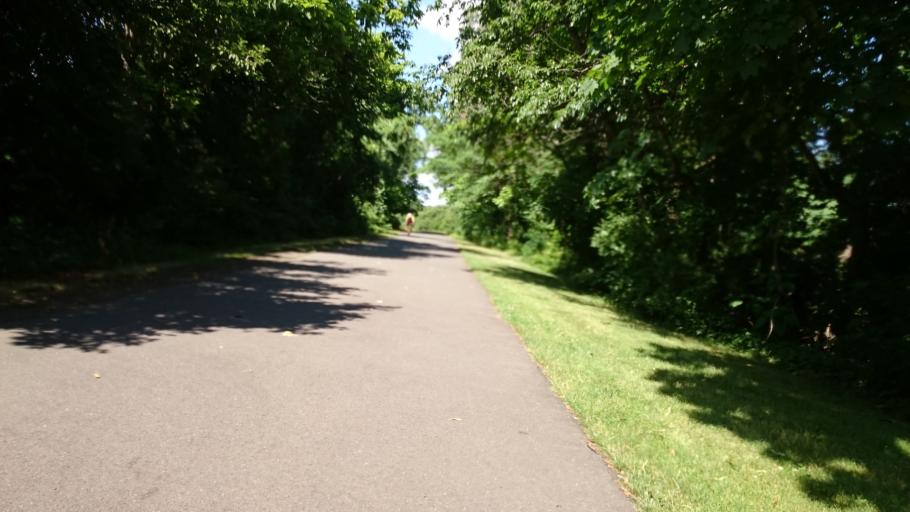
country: US
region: Connecticut
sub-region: New Haven County
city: Hamden
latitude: 41.3697
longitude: -72.9167
